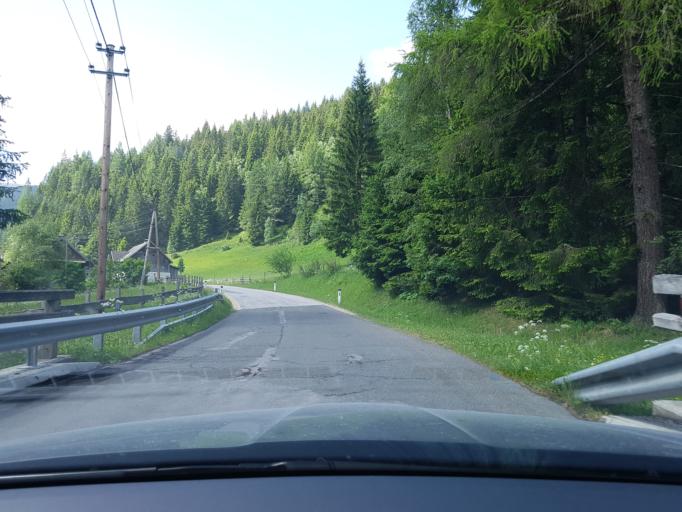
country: AT
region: Salzburg
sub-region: Politischer Bezirk Tamsweg
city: Thomatal
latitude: 47.0491
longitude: 13.7108
